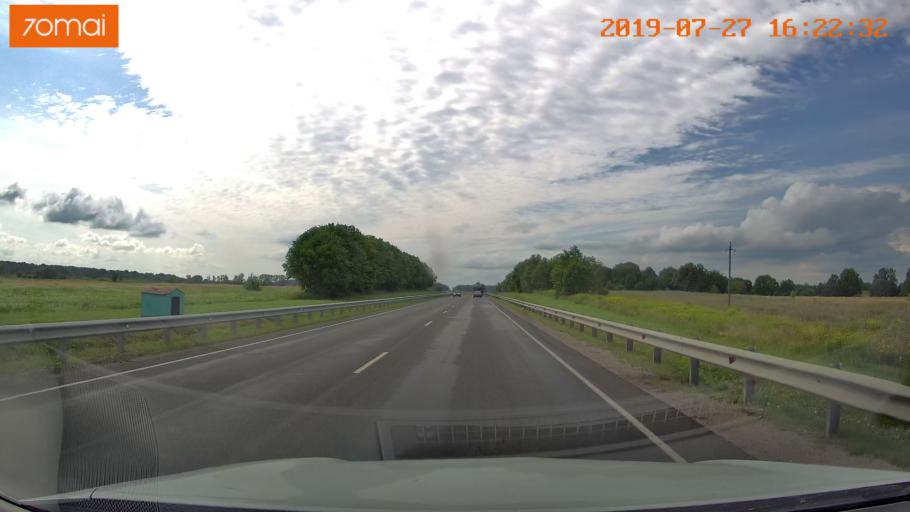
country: RU
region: Kaliningrad
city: Chernyakhovsk
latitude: 54.6285
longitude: 21.4926
